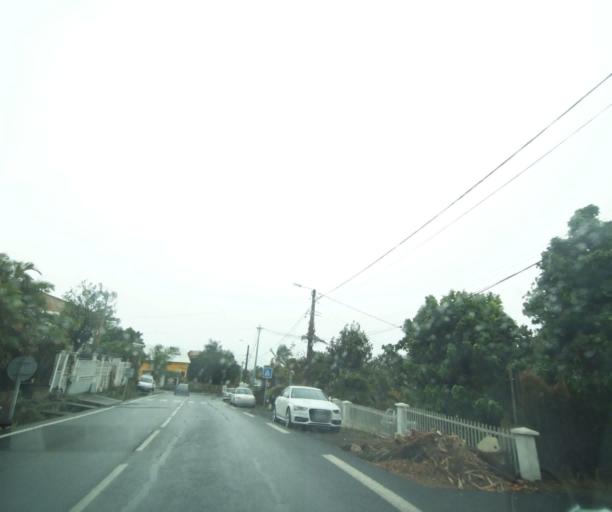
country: RE
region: Reunion
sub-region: Reunion
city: Saint-Paul
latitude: -21.0444
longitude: 55.2634
